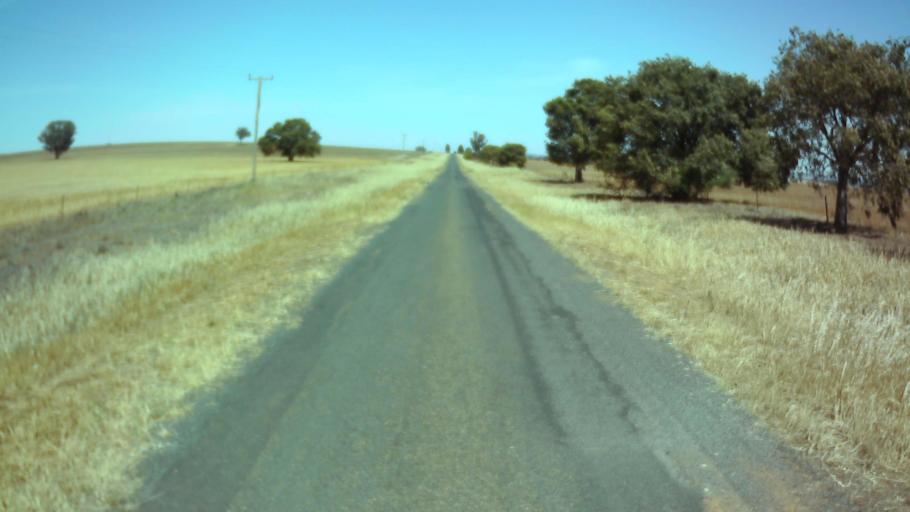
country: AU
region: New South Wales
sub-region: Weddin
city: Grenfell
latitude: -33.8637
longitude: 147.9935
